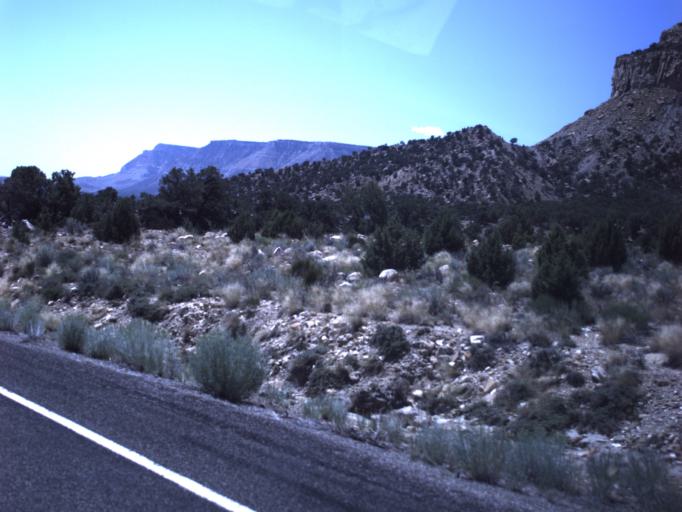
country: US
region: Utah
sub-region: Emery County
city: Orangeville
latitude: 39.3049
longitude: -111.1193
